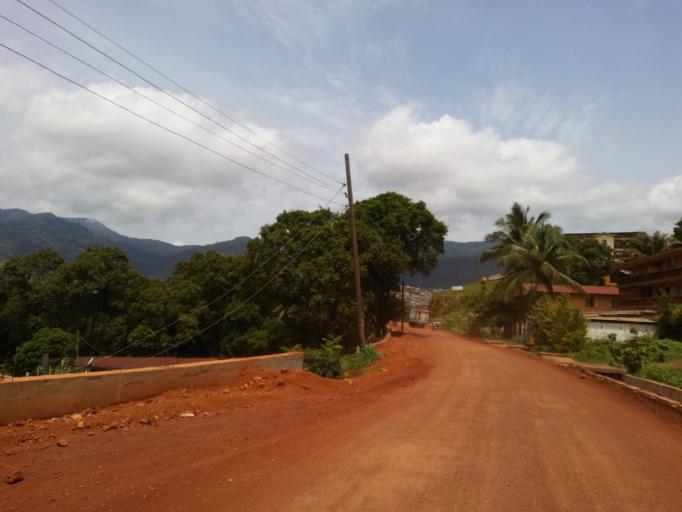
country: SL
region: Western Area
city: Hastings
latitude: 8.4001
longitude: -13.1460
